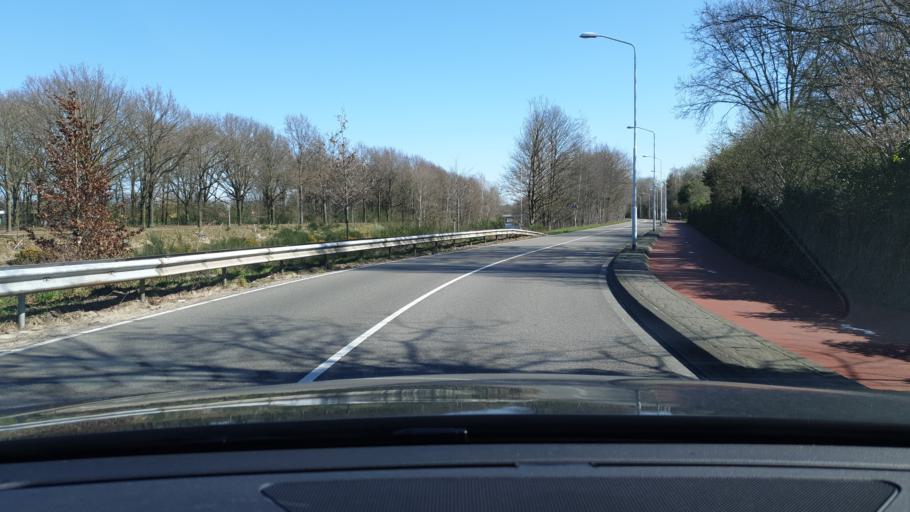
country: NL
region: North Brabant
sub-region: Gemeente Best
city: Best
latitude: 51.4924
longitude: 5.3925
